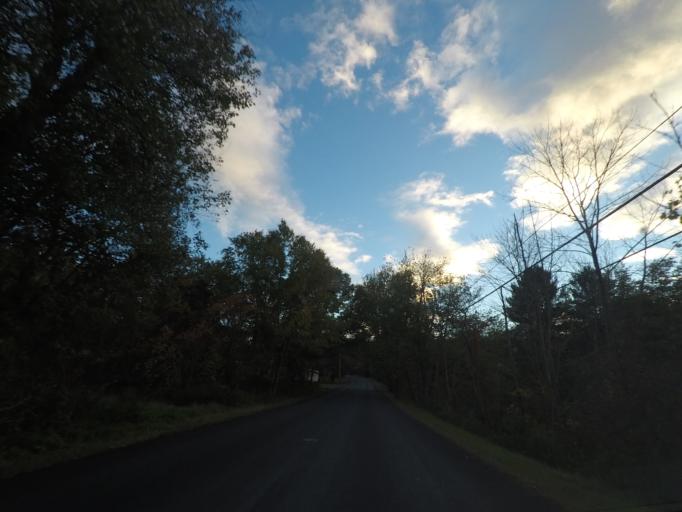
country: US
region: New York
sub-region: Rensselaer County
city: Nassau
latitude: 42.5262
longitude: -73.5883
